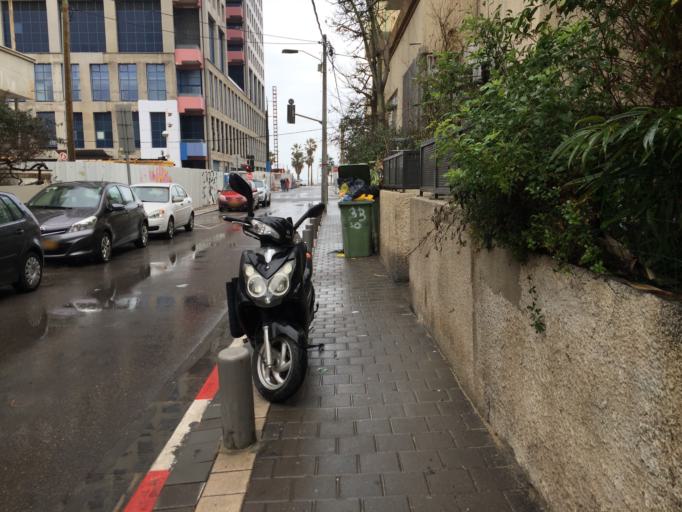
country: IL
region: Tel Aviv
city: Tel Aviv
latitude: 32.0740
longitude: 34.7670
